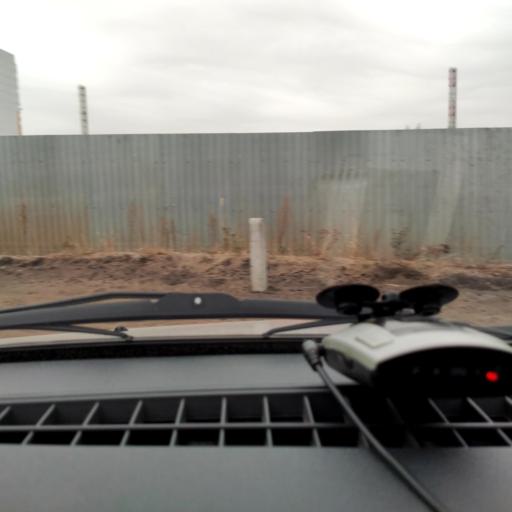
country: RU
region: Voronezj
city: Podgornoye
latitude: 51.7613
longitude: 39.1789
